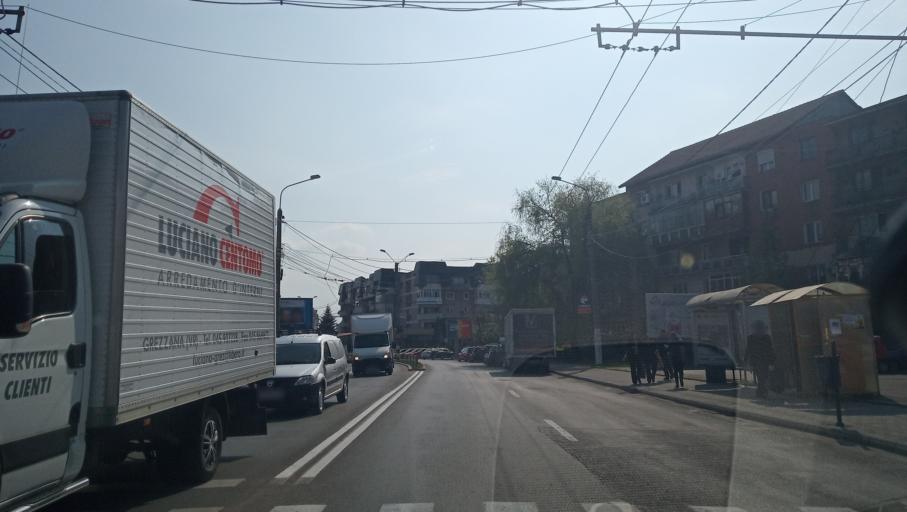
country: RO
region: Gorj
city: Targu Jiu
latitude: 45.0439
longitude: 23.2749
